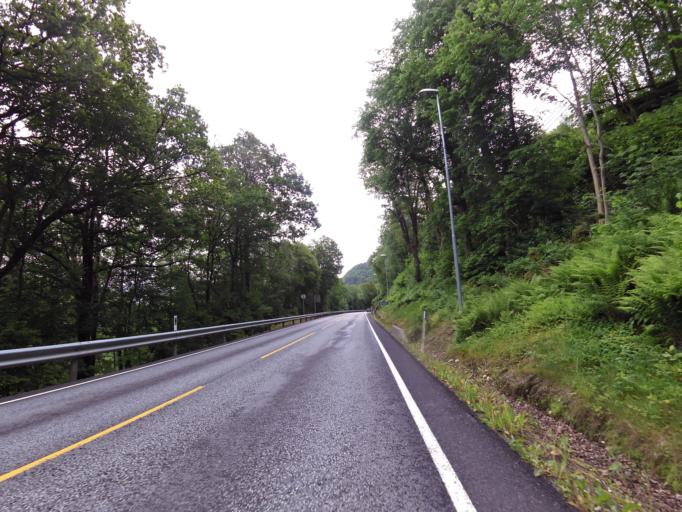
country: NO
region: Vest-Agder
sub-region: Lyngdal
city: Lyngdal
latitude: 58.1130
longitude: 6.9468
